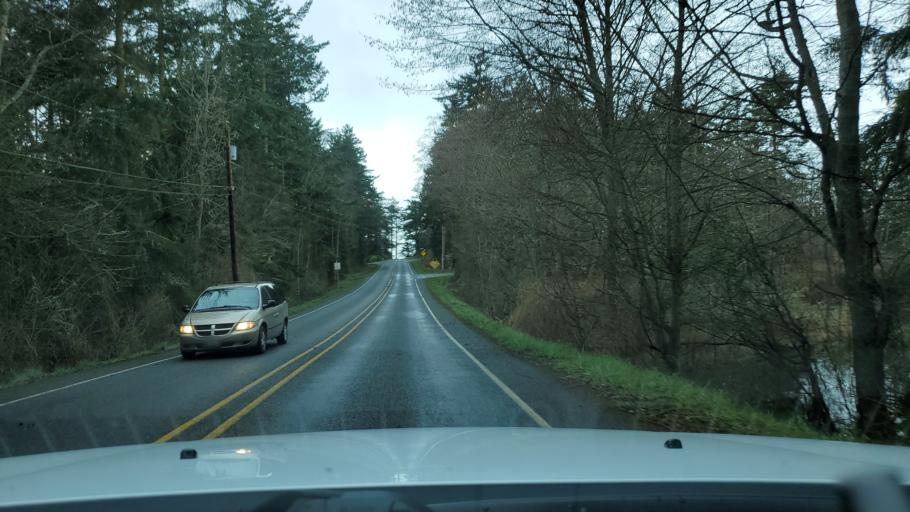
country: US
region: Washington
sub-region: Island County
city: Coupeville
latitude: 48.2319
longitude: -122.7621
